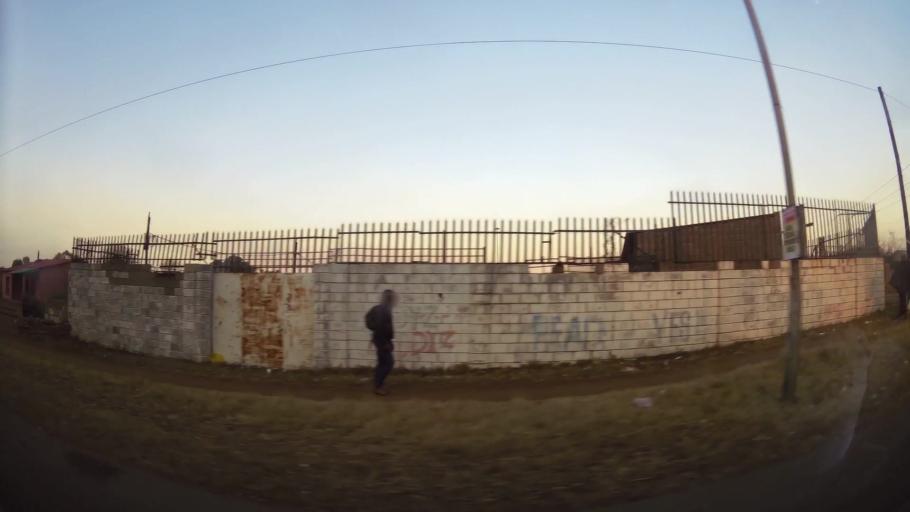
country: ZA
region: Gauteng
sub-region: Ekurhuleni Metropolitan Municipality
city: Springs
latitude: -26.2835
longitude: 28.4047
